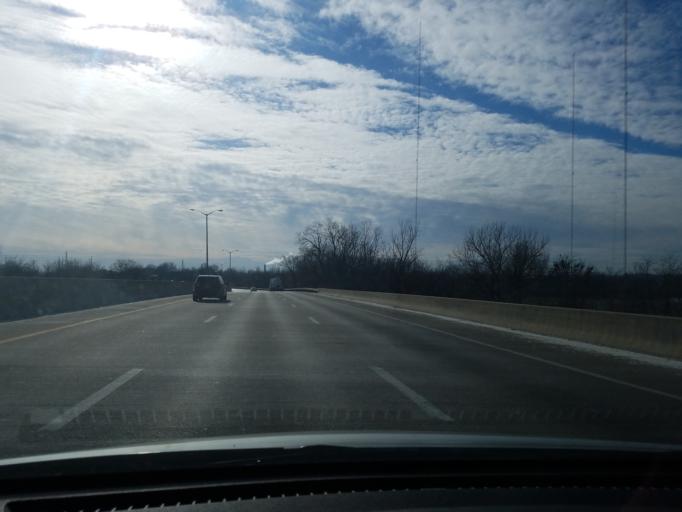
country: US
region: Kentucky
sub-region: Jefferson County
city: Shively
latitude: 38.2328
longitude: -85.8201
